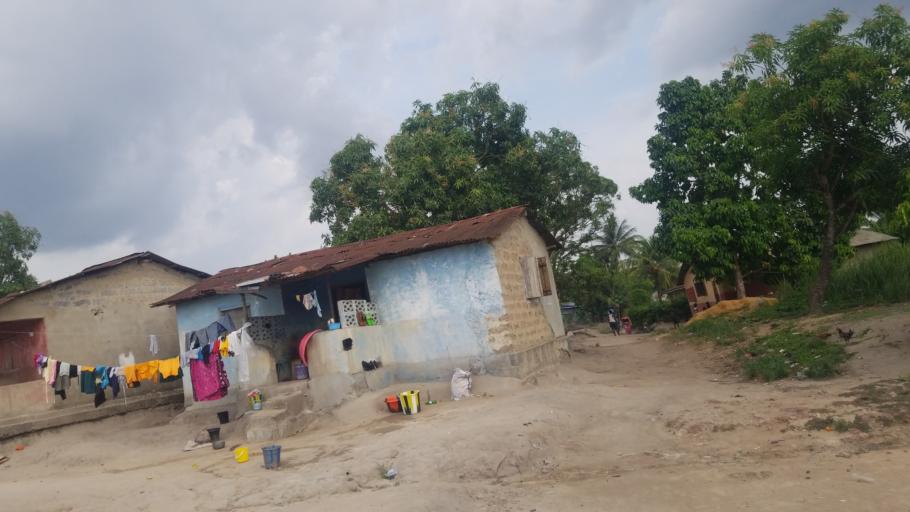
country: SL
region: Western Area
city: Waterloo
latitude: 8.3239
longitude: -13.0522
